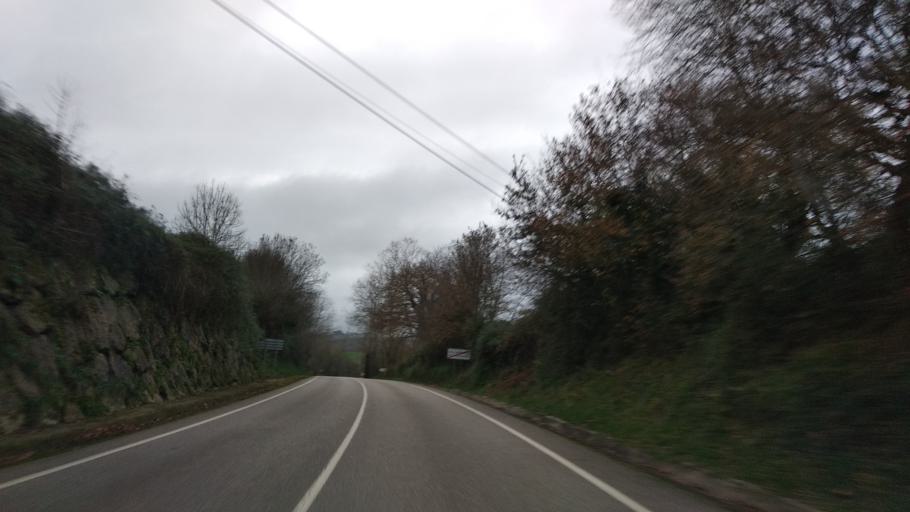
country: ES
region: Cantabria
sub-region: Provincia de Cantabria
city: Entrambasaguas
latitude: 43.4173
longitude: -3.7035
